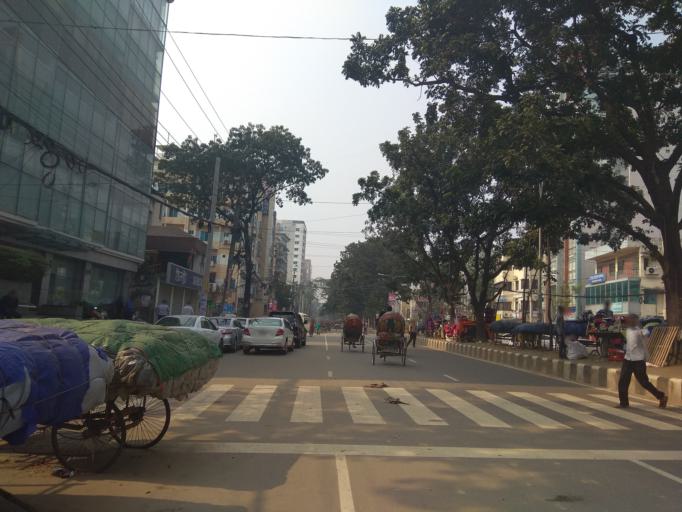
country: BD
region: Dhaka
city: Tungi
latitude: 23.8676
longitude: 90.3981
